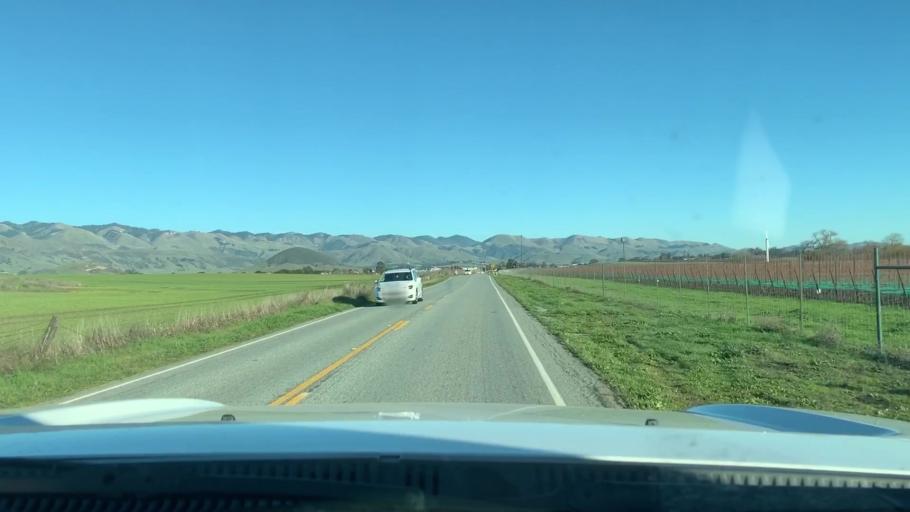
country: US
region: California
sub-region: San Luis Obispo County
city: San Luis Obispo
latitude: 35.2359
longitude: -120.6716
